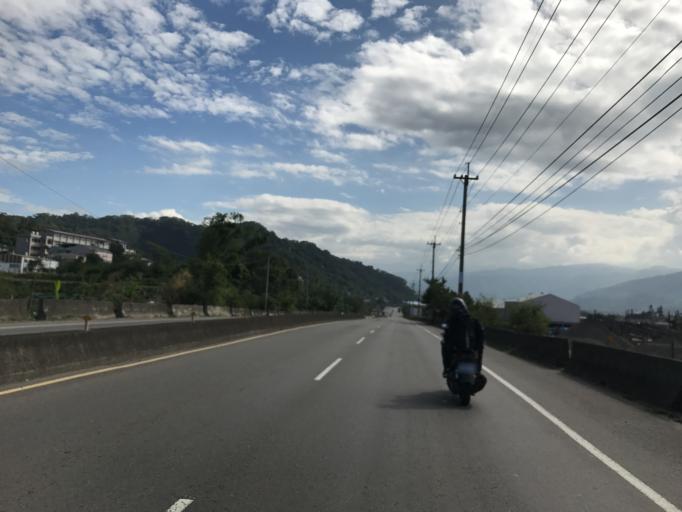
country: TW
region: Taiwan
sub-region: Hsinchu
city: Zhubei
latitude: 24.7471
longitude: 121.0997
